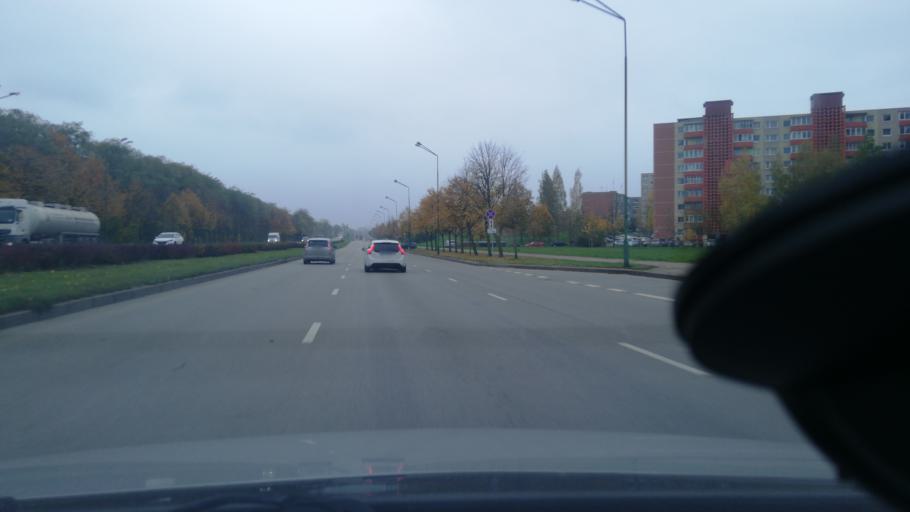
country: LT
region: Klaipedos apskritis
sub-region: Klaipeda
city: Klaipeda
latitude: 55.6750
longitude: 21.1940
